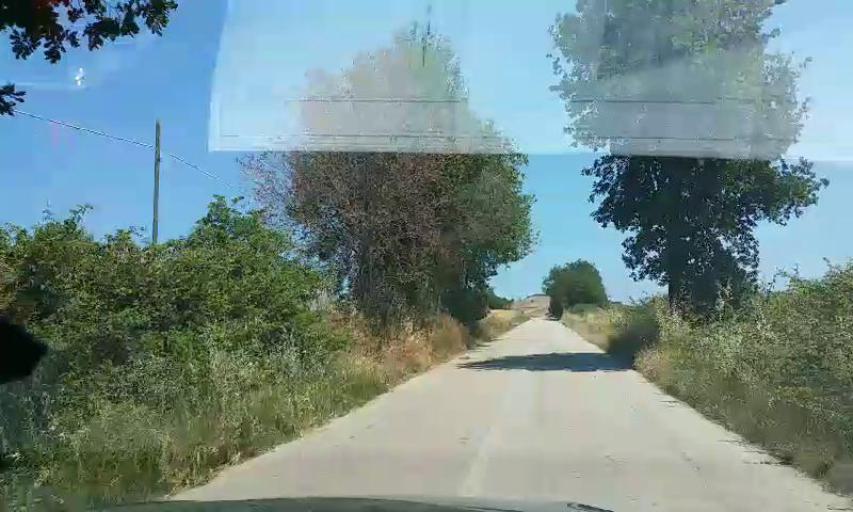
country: IT
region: Molise
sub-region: Provincia di Campobasso
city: Guglionesi
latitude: 41.9445
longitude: 14.8984
